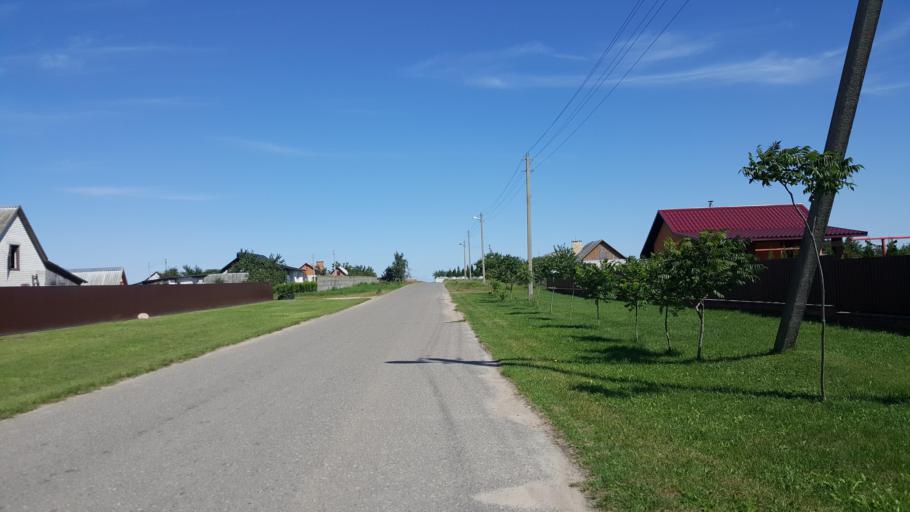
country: BY
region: Brest
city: Charnawchytsy
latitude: 52.2735
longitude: 23.7585
